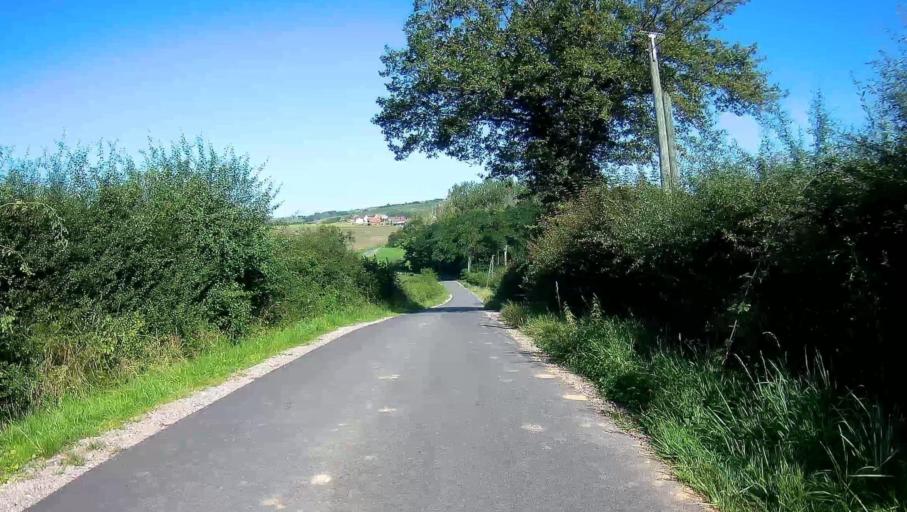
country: FR
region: Bourgogne
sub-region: Departement de Saone-et-Loire
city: Couches
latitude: 46.8367
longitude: 4.5857
